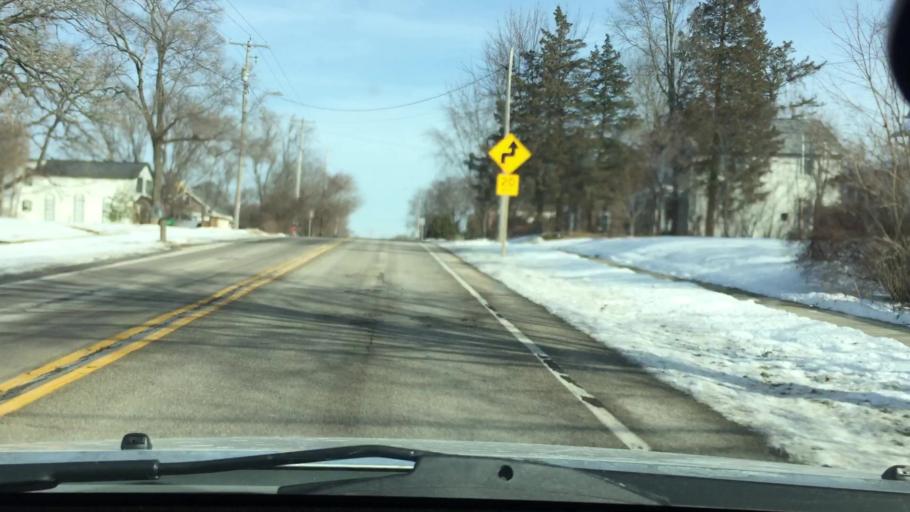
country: US
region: Wisconsin
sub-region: Waukesha County
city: Eagle
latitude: 42.8774
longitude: -88.4780
